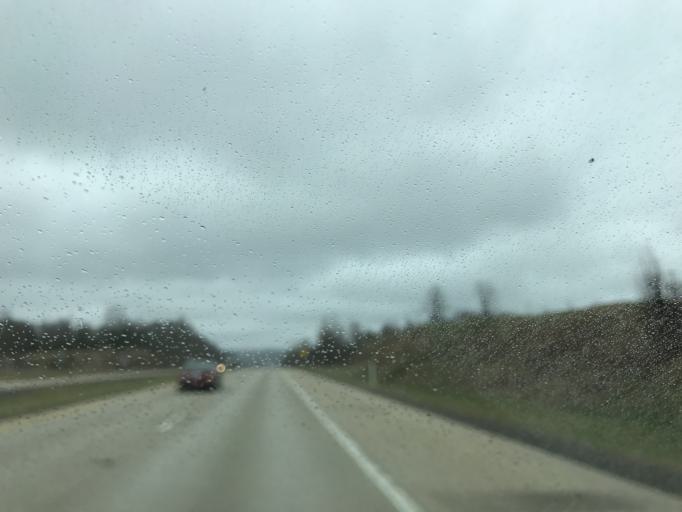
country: US
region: West Virginia
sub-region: Raleigh County
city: Daniels
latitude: 37.7732
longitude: -81.0644
